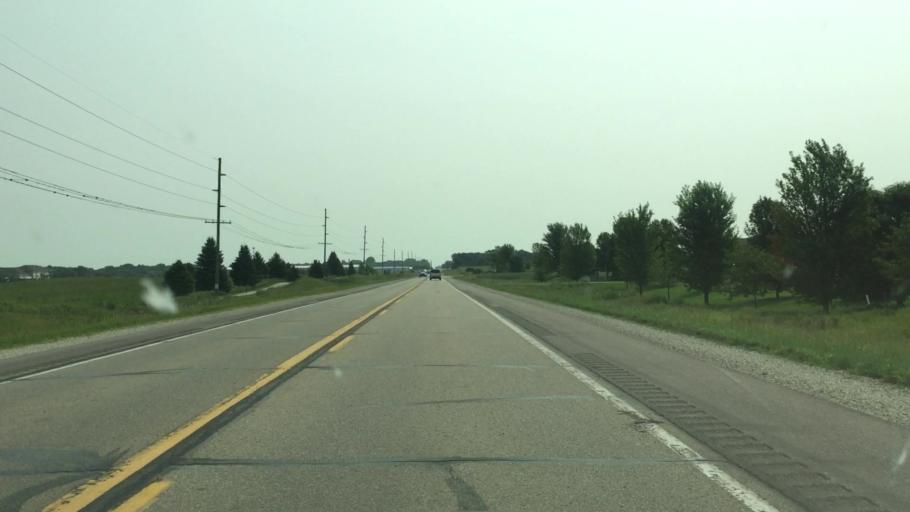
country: US
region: Iowa
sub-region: Dickinson County
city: Milford
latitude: 43.3424
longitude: -95.1694
